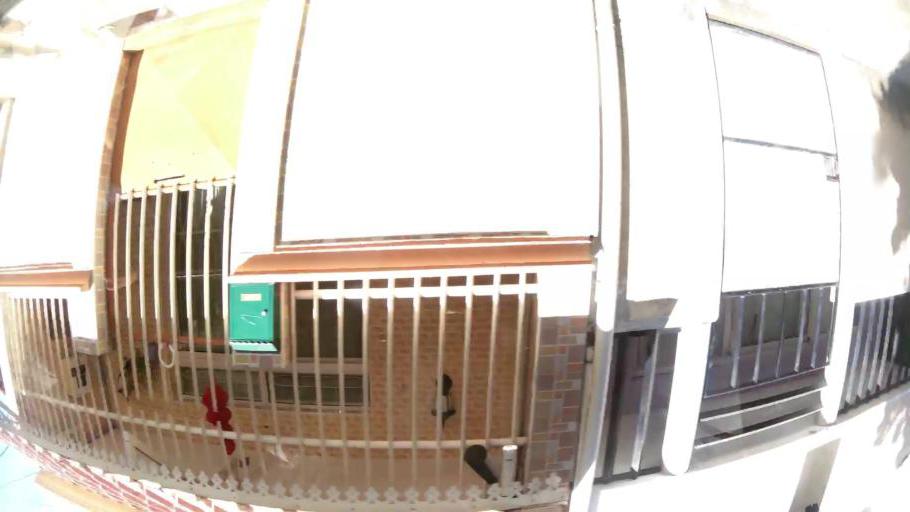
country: MU
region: Pamplemousses
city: Le Hochet
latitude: -20.1448
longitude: 57.5194
